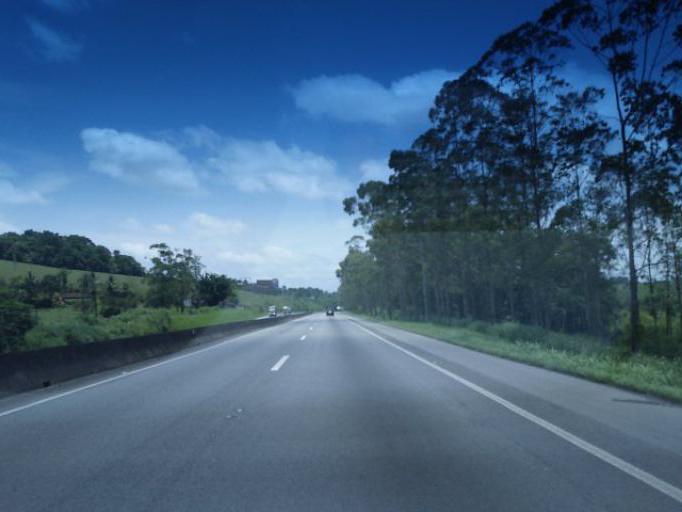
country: BR
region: Sao Paulo
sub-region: Registro
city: Registro
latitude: -24.4167
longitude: -47.7623
